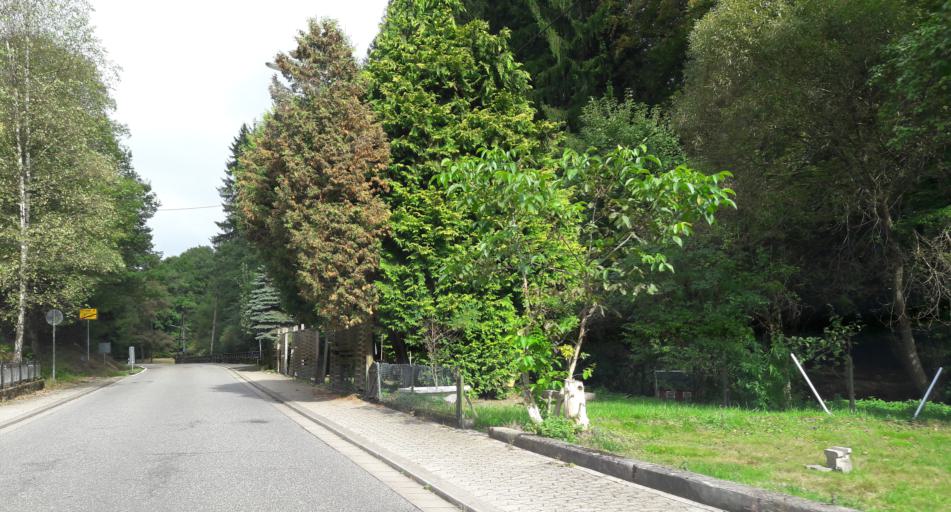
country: DE
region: Rheinland-Pfalz
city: Hahnweiler
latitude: 49.5179
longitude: 7.2109
